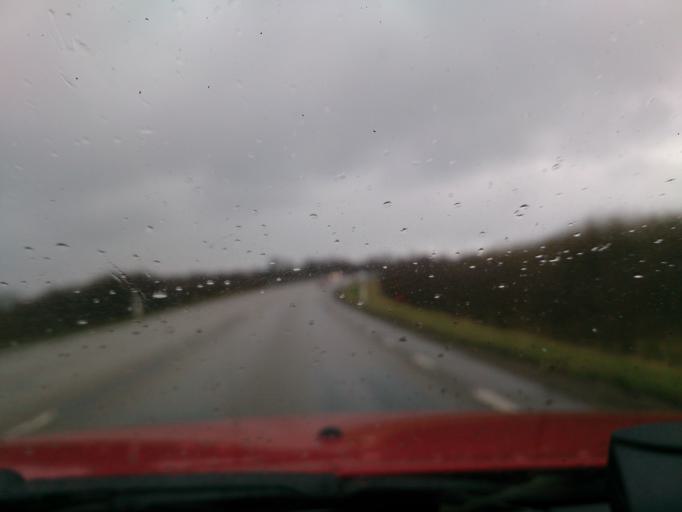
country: SE
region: Skane
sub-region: Ystads Kommun
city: Ystad
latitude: 55.4294
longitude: 13.7737
